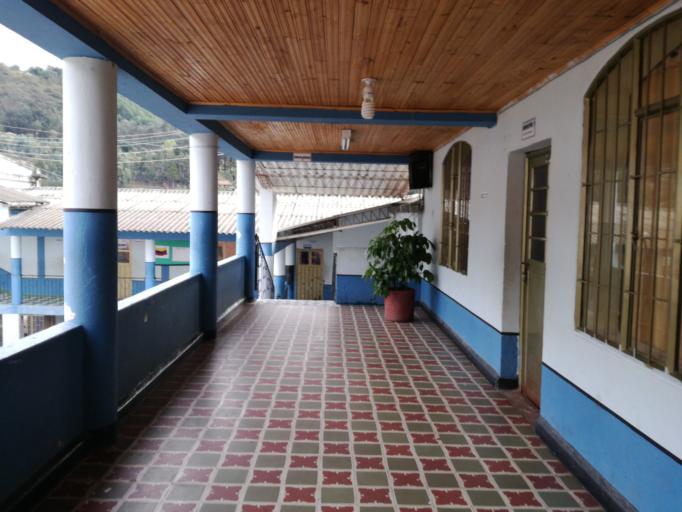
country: CO
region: Boyaca
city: Socha Viejo
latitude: 5.9963
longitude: -72.6916
